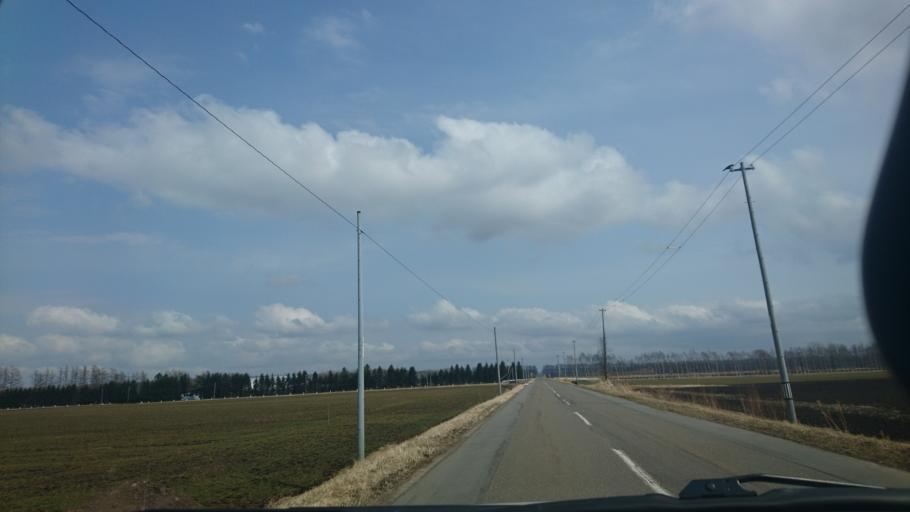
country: JP
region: Hokkaido
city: Otofuke
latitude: 43.2064
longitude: 143.2791
